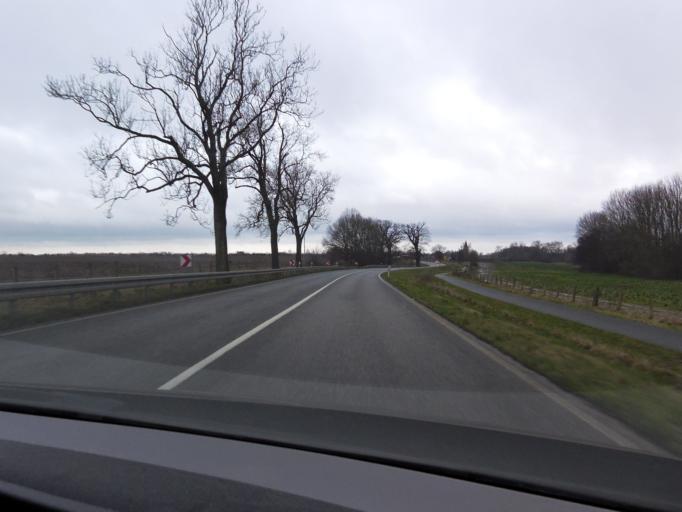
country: DE
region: Mecklenburg-Vorpommern
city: Klutz
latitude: 53.9754
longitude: 11.1801
